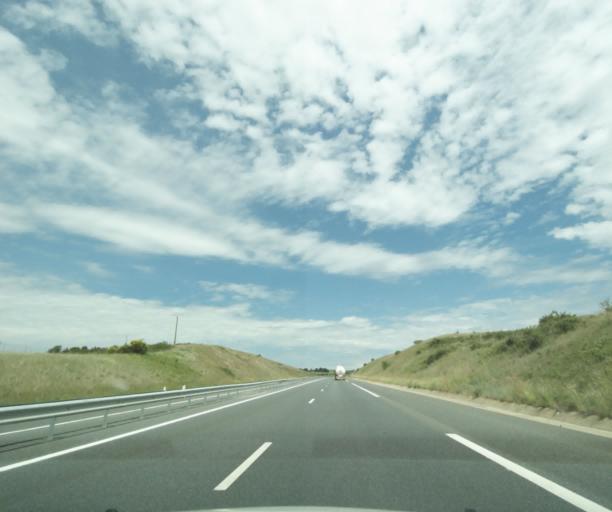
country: FR
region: Midi-Pyrenees
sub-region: Departement de l'Aveyron
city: Creissels
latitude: 44.1136
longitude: 3.0297
